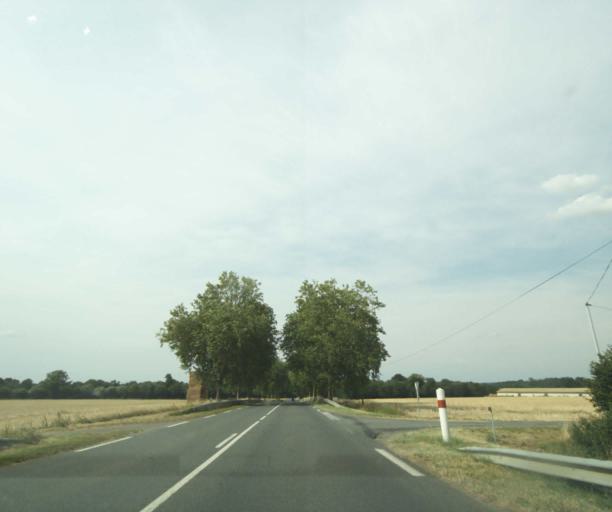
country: FR
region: Centre
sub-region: Departement d'Indre-et-Loire
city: Saint-Christophe-sur-le-Nais
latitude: 47.6240
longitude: 0.5041
